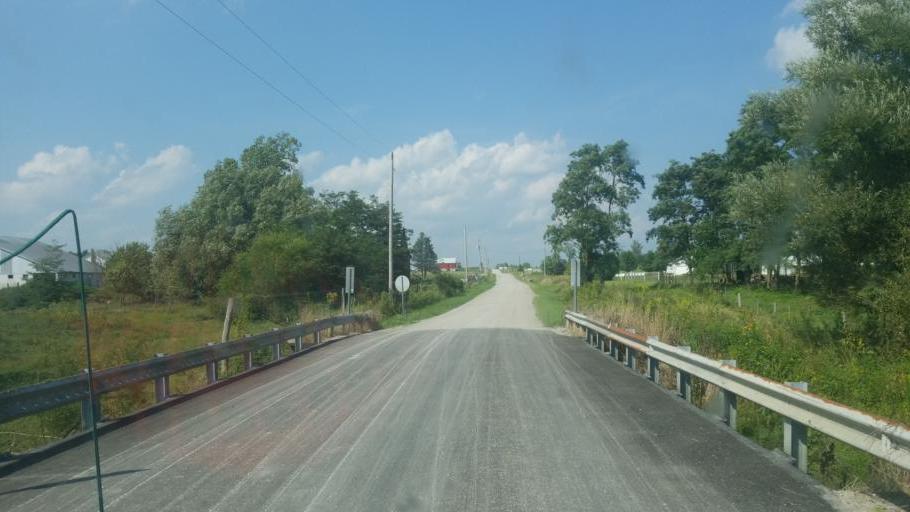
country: US
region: Ohio
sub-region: Wayne County
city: West Salem
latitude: 41.0448
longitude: -82.1449
